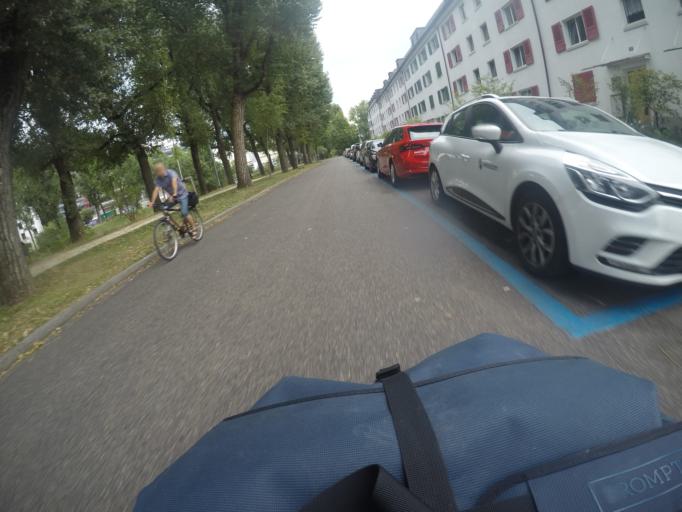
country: FR
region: Alsace
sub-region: Departement du Haut-Rhin
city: Village-Neuf
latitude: 47.5789
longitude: 7.5942
